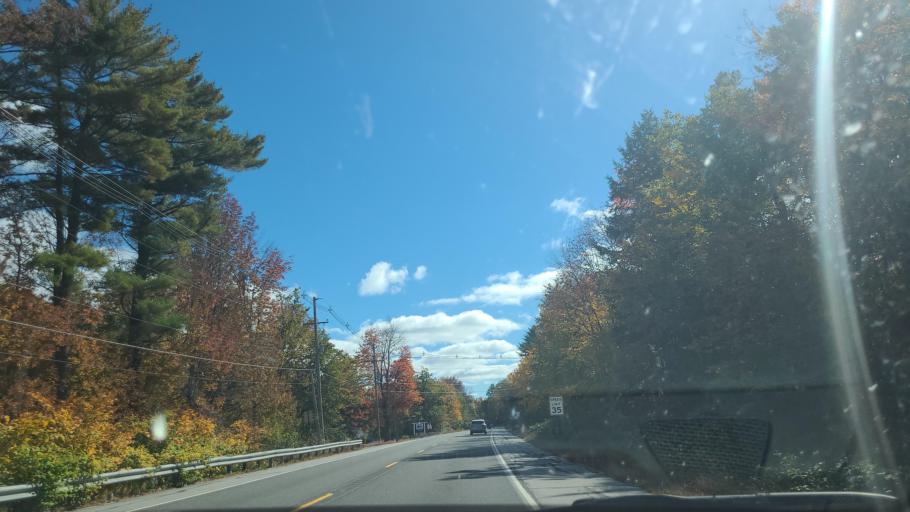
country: US
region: Maine
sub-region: Cumberland County
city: Bridgton
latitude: 43.9768
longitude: -70.6205
